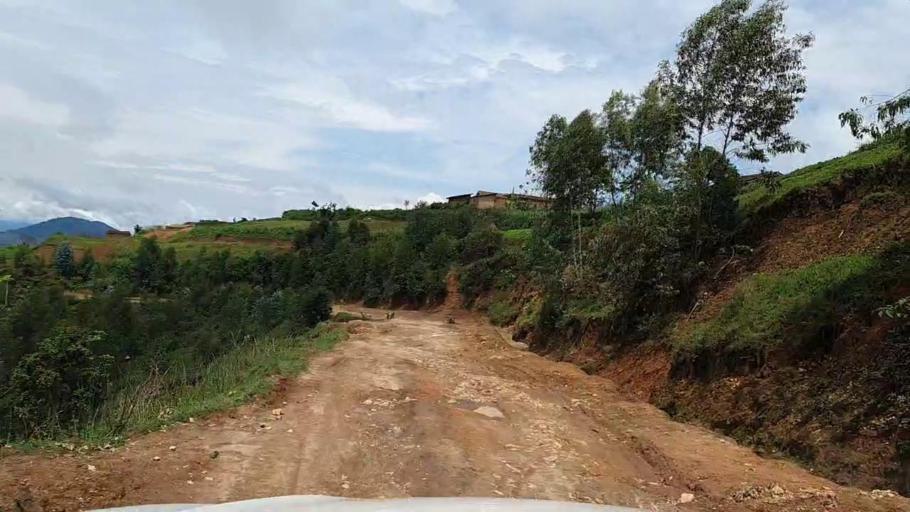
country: RW
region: Southern Province
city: Gikongoro
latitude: -2.3425
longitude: 29.5124
